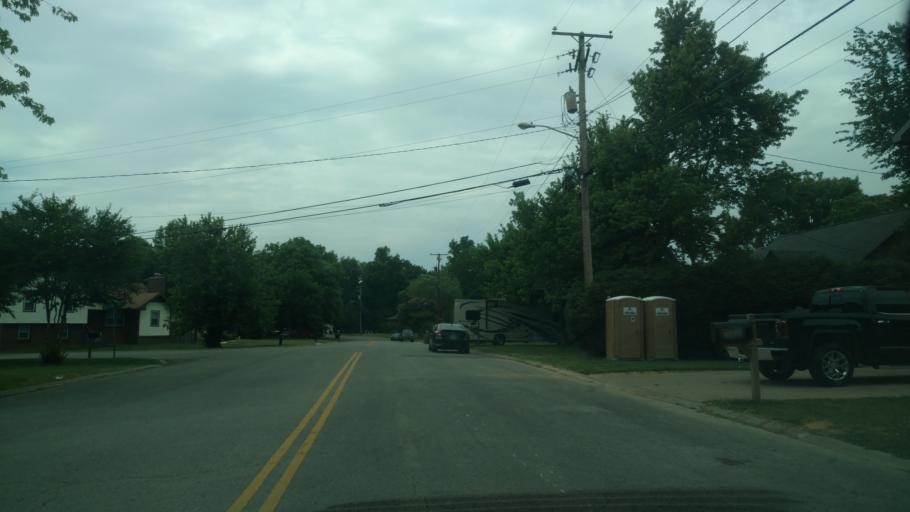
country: US
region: Tennessee
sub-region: Davidson County
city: Lakewood
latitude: 36.2028
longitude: -86.6982
